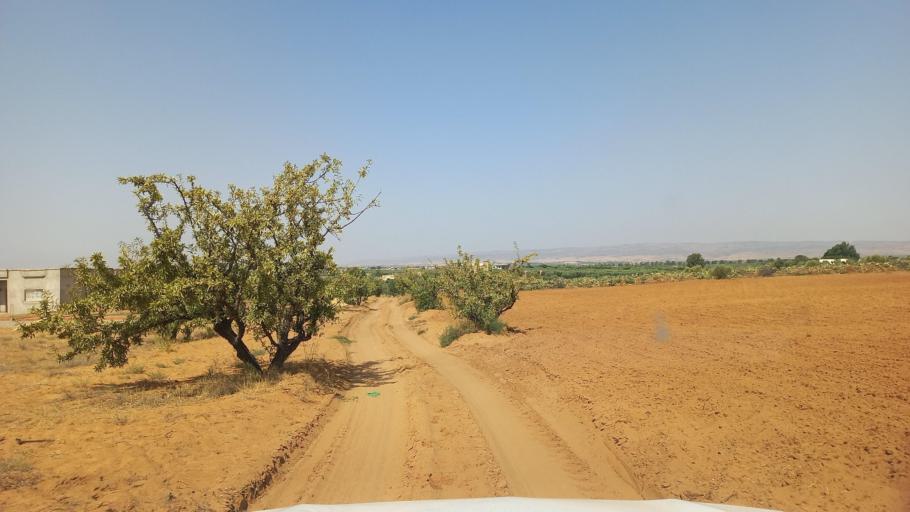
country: TN
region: Al Qasrayn
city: Kasserine
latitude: 35.2472
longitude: 9.0548
